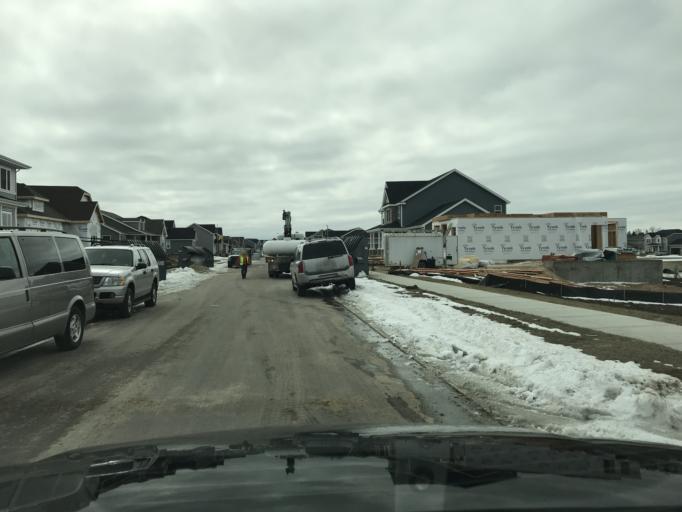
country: US
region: Wisconsin
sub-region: Dane County
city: Monona
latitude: 43.0955
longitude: -89.2724
